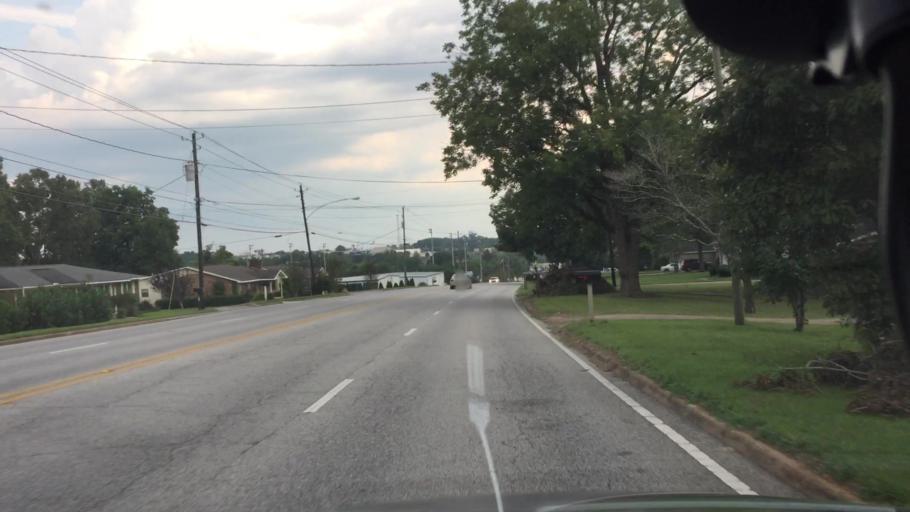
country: US
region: Alabama
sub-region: Coffee County
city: Enterprise
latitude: 31.3351
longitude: -85.8390
